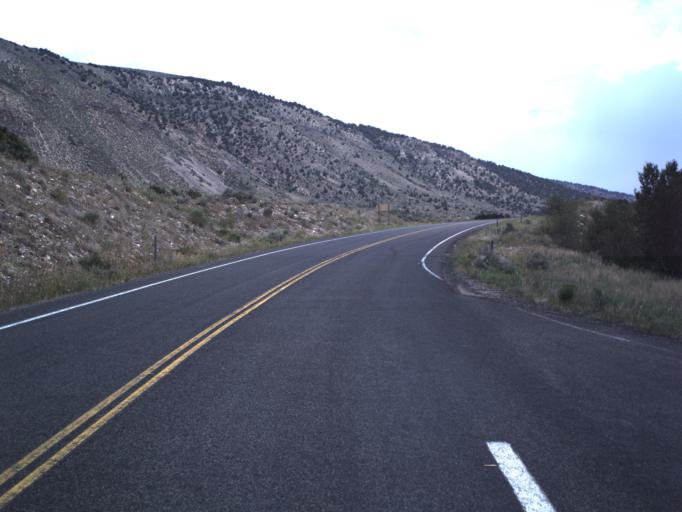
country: US
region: Utah
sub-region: Summit County
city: Francis
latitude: 40.4629
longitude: -110.8317
